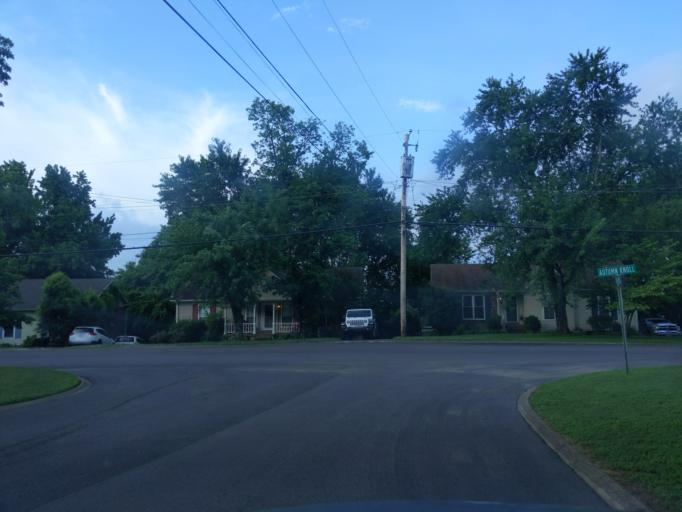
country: US
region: Tennessee
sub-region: Wilson County
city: Green Hill
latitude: 36.1869
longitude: -86.5994
